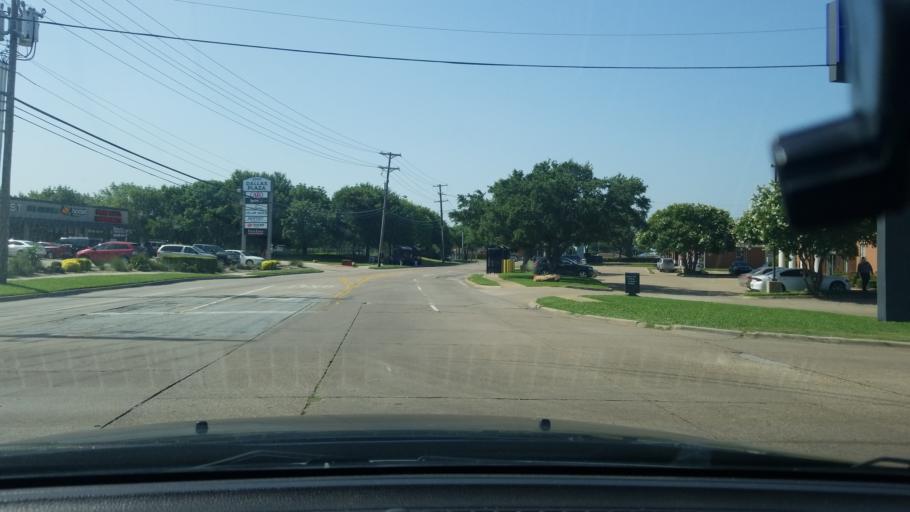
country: US
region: Texas
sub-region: Dallas County
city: Balch Springs
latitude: 32.7943
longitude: -96.6915
